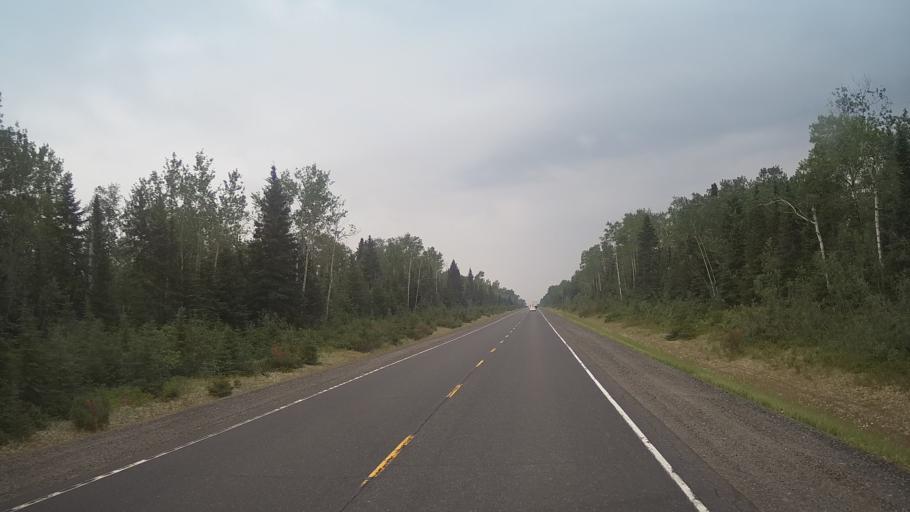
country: CA
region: Ontario
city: Greenstone
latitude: 49.2246
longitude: -88.1915
